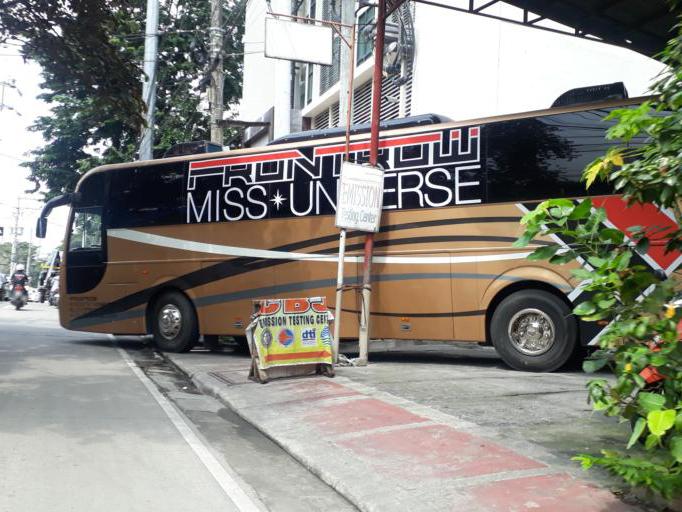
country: PH
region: Metro Manila
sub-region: San Juan
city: San Juan
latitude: 14.6161
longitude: 121.0509
